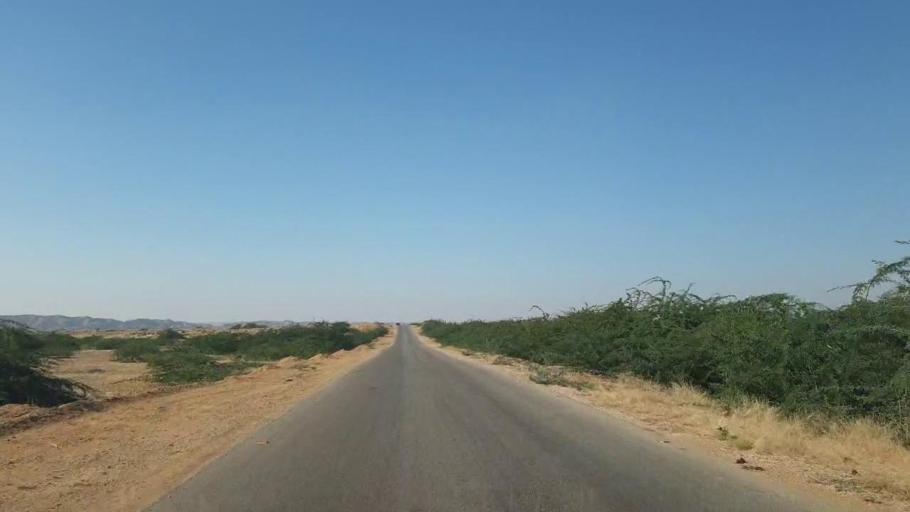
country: PK
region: Sindh
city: Malir Cantonment
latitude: 25.2778
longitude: 67.5869
